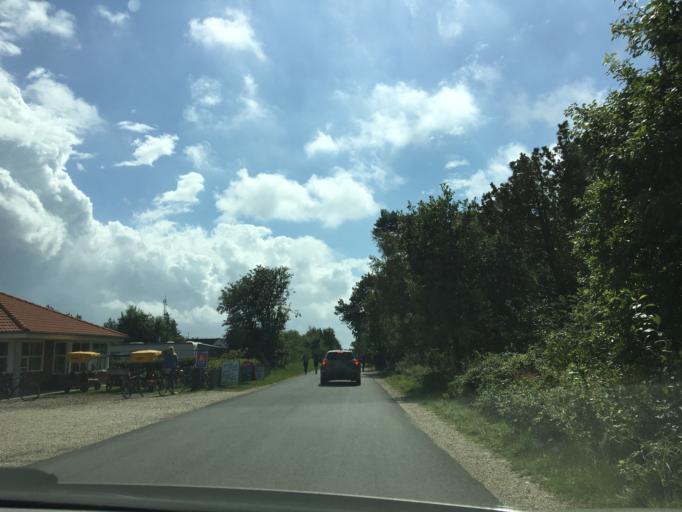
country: DK
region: South Denmark
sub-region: Varde Kommune
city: Oksbol
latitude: 55.7340
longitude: 8.2222
